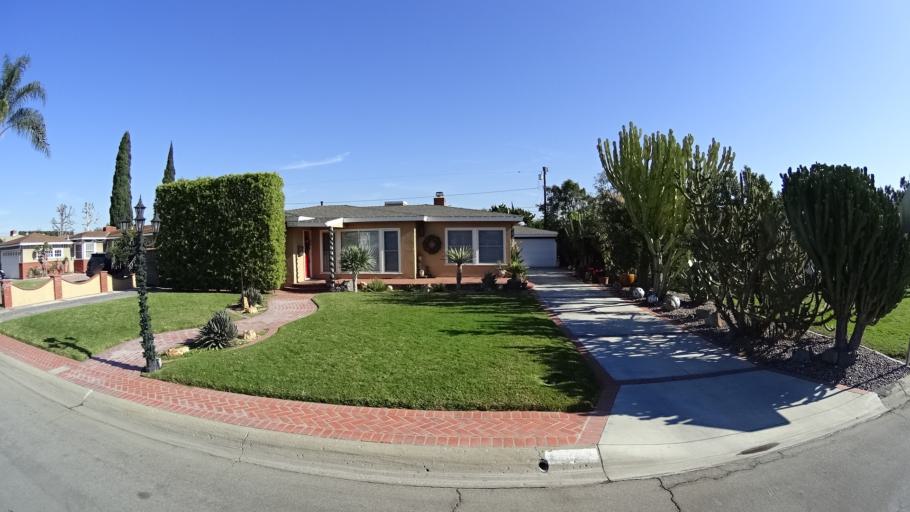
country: US
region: California
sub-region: Orange County
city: Garden Grove
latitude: 33.7840
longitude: -117.9351
